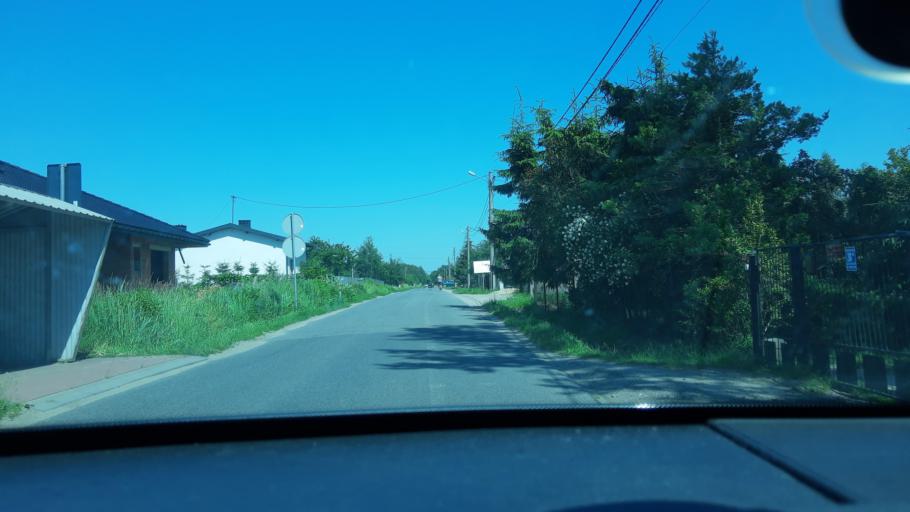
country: PL
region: Lodz Voivodeship
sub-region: Powiat zdunskowolski
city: Zdunska Wola
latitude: 51.6177
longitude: 18.9782
